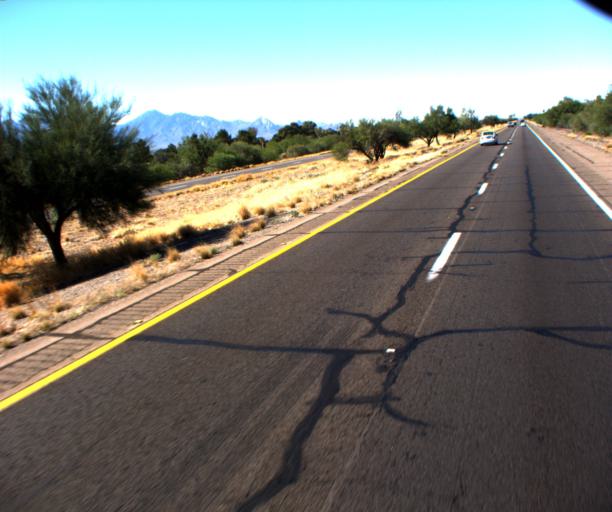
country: US
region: Arizona
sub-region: Pima County
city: Green Valley
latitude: 31.8806
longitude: -110.9889
